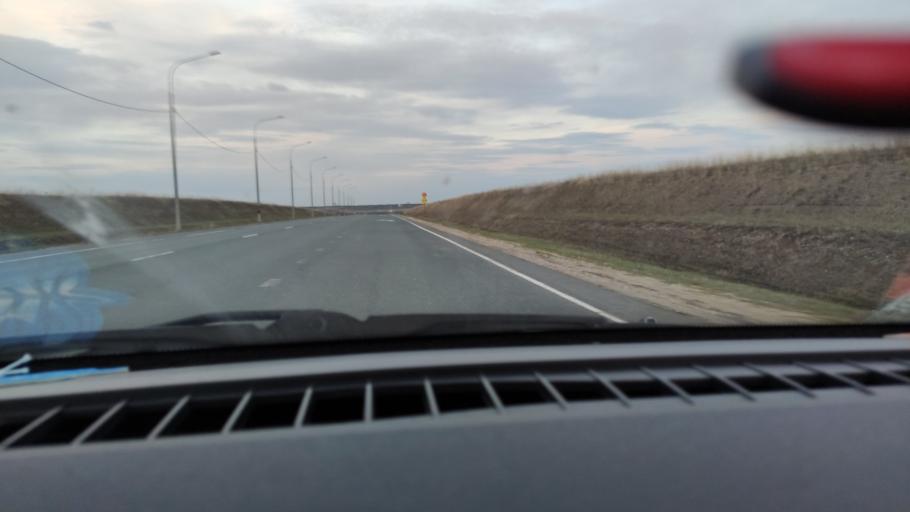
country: RU
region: Saratov
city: Yelshanka
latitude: 51.8306
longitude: 46.4469
